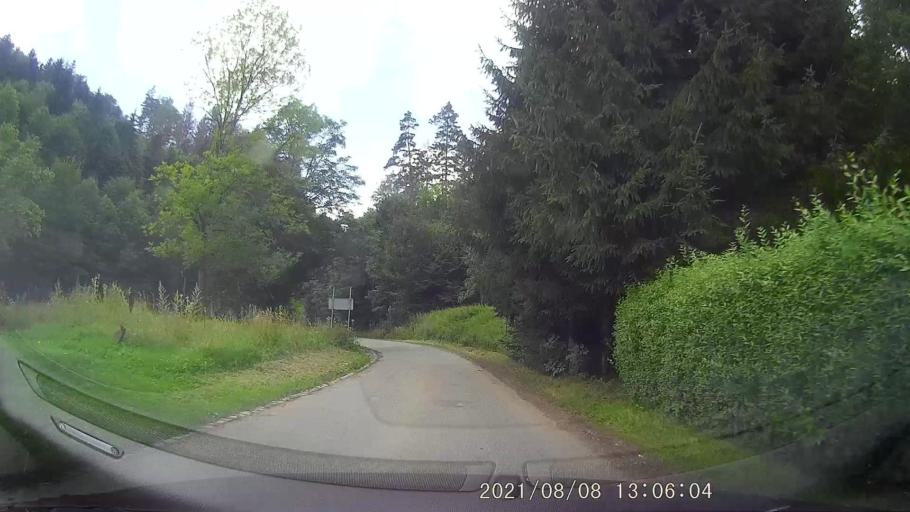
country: PL
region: Lower Silesian Voivodeship
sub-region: Powiat klodzki
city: Lewin Klodzki
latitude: 50.4294
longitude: 16.2984
